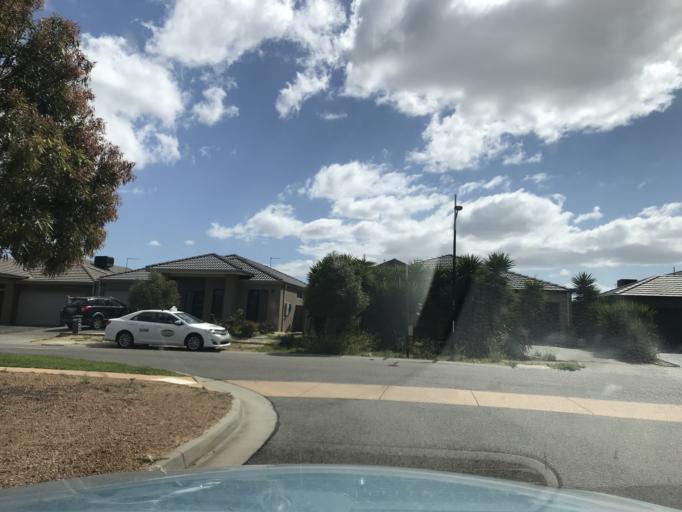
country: AU
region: Victoria
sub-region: Wyndham
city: Williams Landing
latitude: -37.8592
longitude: 144.7337
